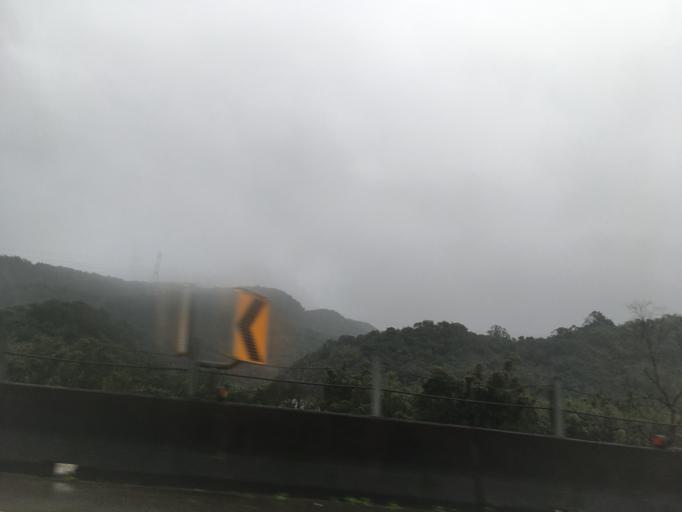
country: TW
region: Taiwan
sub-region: Keelung
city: Keelung
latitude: 25.0237
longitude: 121.8875
